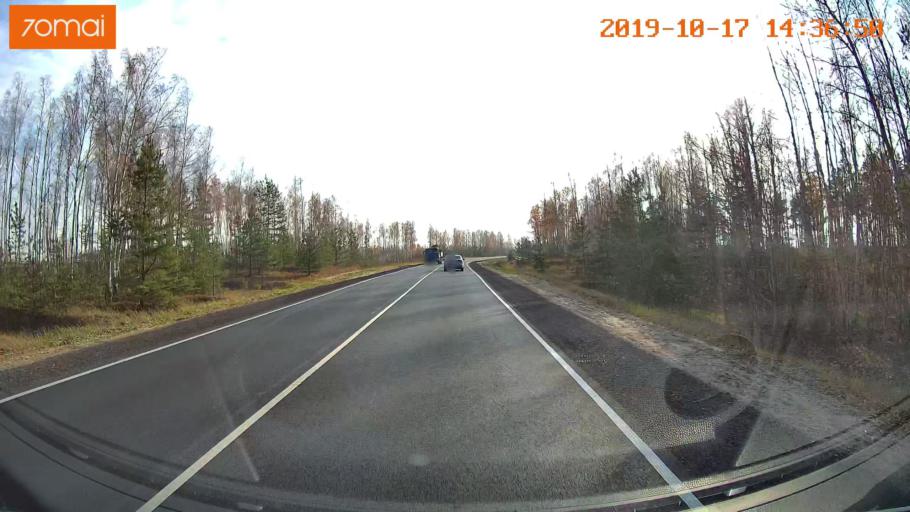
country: RU
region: Rjazan
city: Solotcha
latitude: 54.8862
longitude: 40.0002
